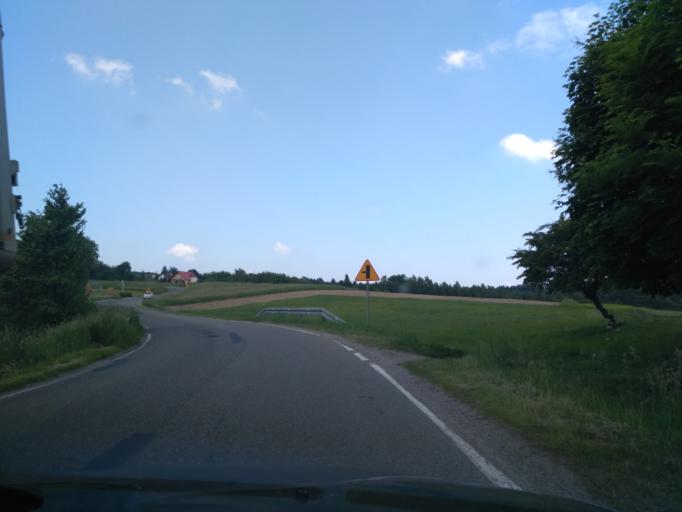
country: PL
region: Subcarpathian Voivodeship
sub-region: Powiat lancucki
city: Handzlowka
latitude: 49.9771
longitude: 22.1910
